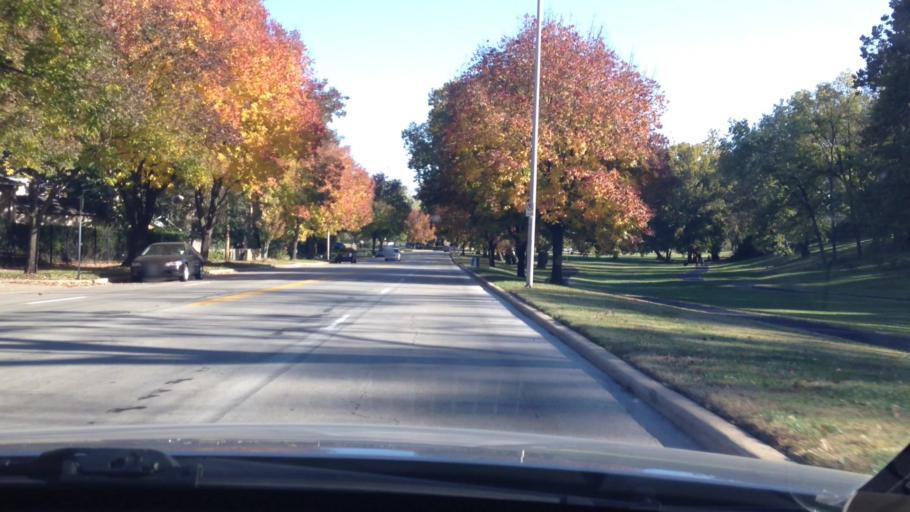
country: US
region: Kansas
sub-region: Johnson County
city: Westwood
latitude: 39.0468
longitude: -94.5763
